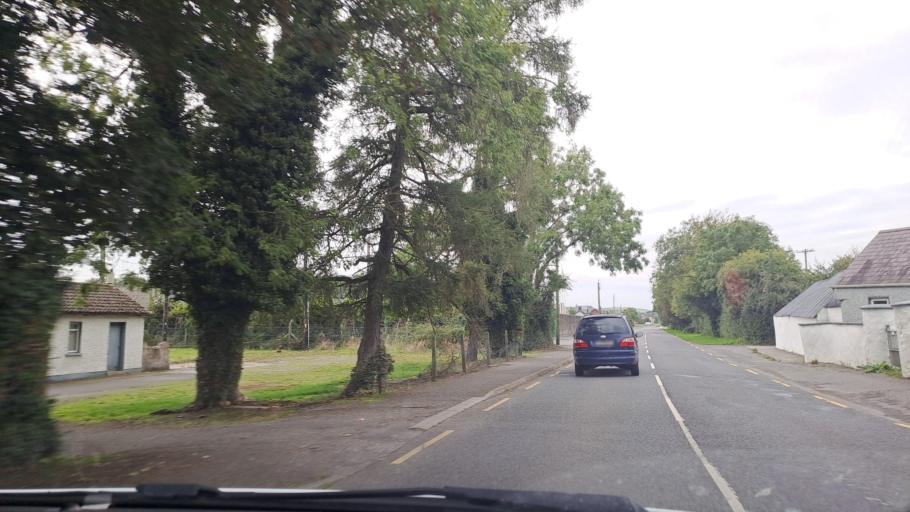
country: IE
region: Ulster
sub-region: County Monaghan
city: Carrickmacross
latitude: 53.9847
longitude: -6.7195
